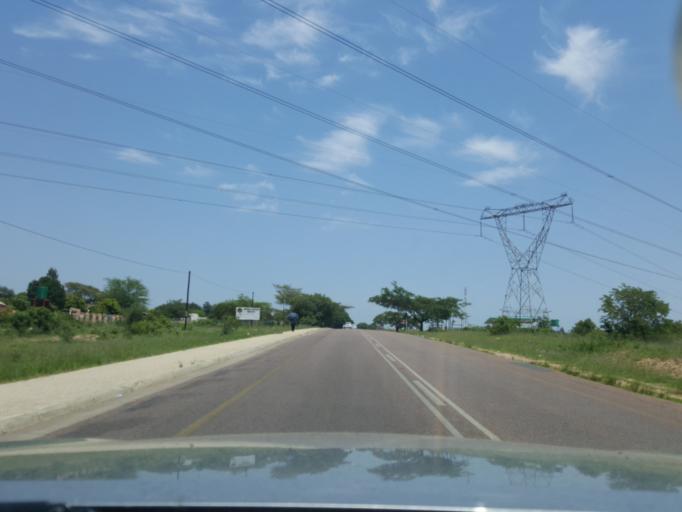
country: ZA
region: Limpopo
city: Thulamahashi
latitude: -24.7793
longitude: 31.0531
